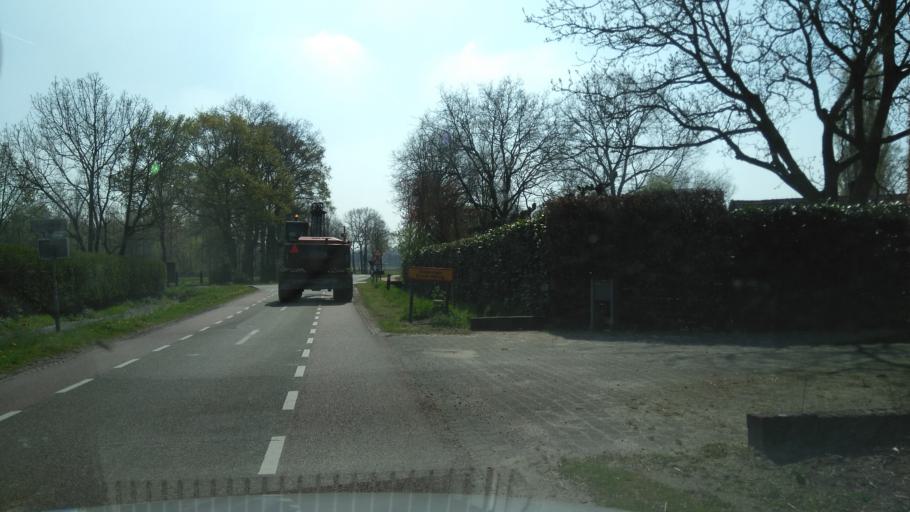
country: BE
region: Flanders
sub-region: Provincie Antwerpen
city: Baarle-Hertog
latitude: 51.4142
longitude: 4.9012
